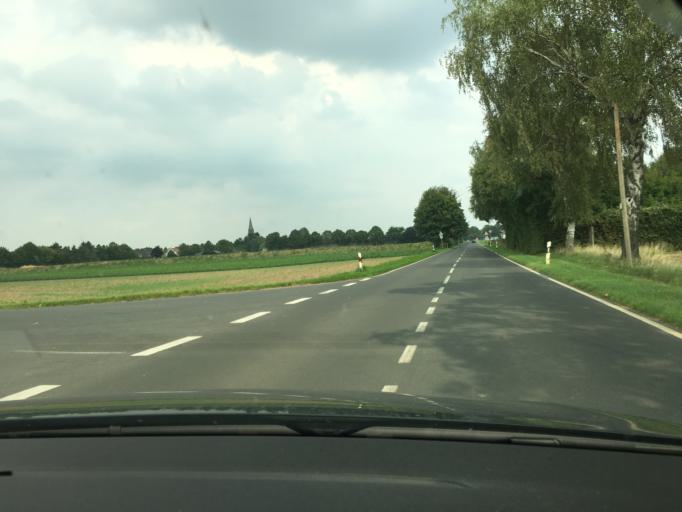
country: DE
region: North Rhine-Westphalia
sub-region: Regierungsbezirk Koln
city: Elsdorf
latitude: 50.8759
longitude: 6.5983
